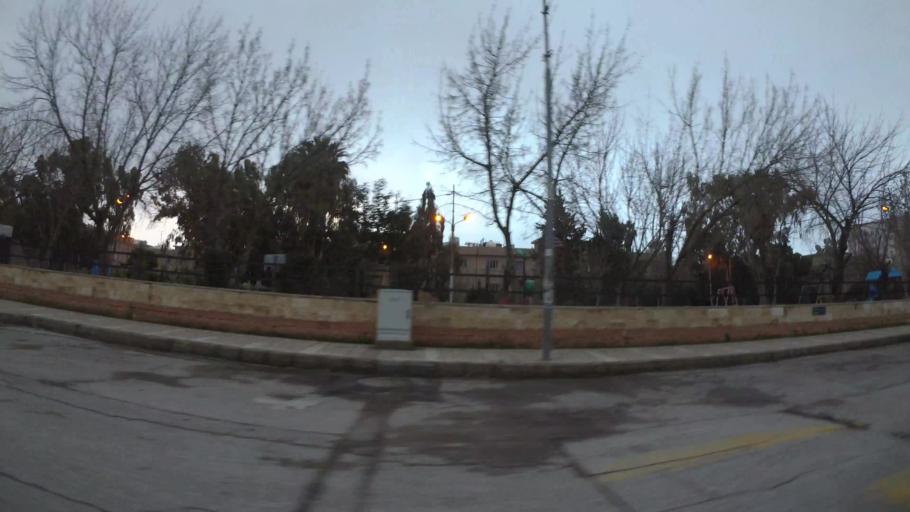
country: JO
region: Amman
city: Al Jubayhah
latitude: 31.9694
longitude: 35.8811
